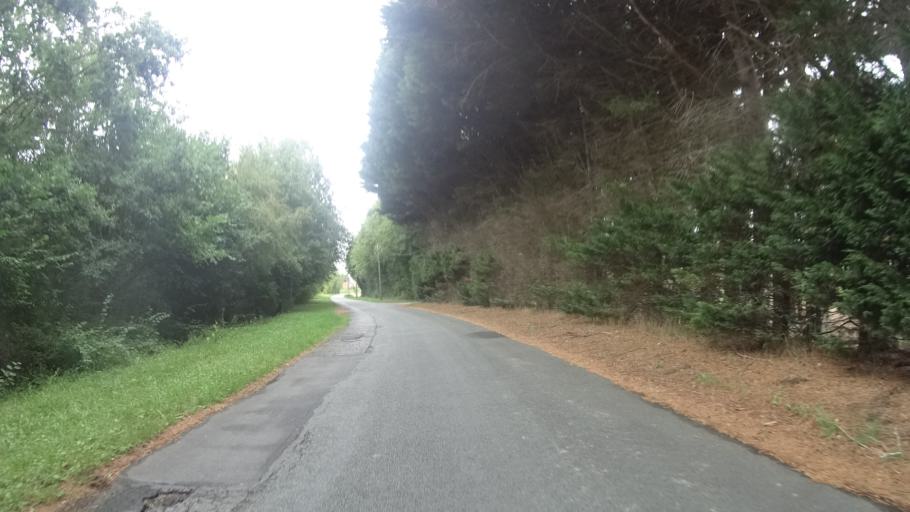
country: FR
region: Picardie
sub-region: Departement de l'Oise
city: Chiry-Ourscamp
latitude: 49.5311
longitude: 2.9533
